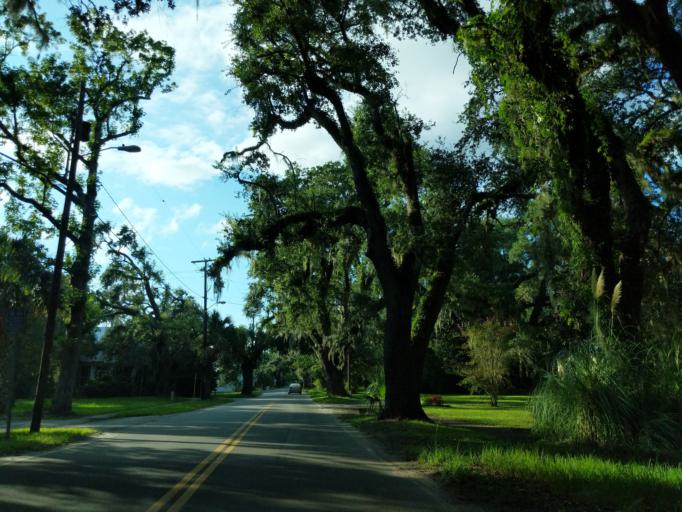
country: US
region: South Carolina
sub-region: Charleston County
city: Awendaw
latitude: 33.0882
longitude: -79.4612
